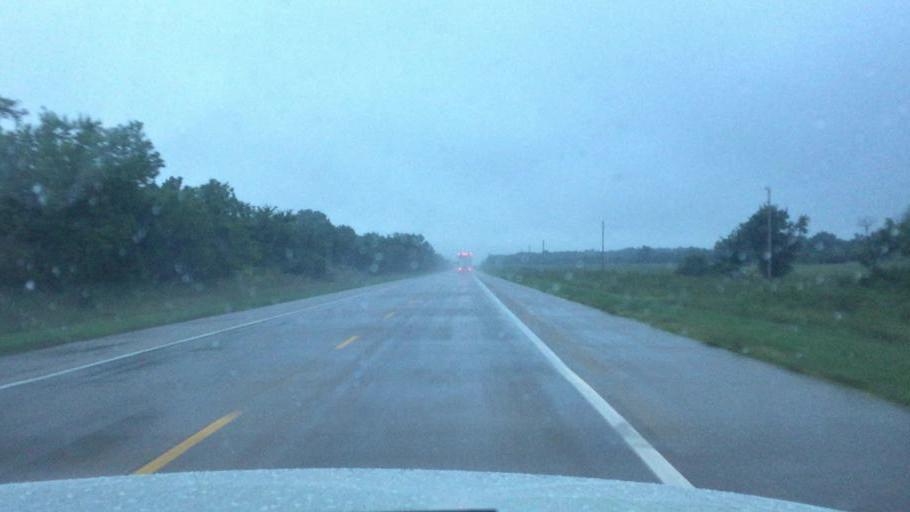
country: US
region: Kansas
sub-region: Neosho County
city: Chanute
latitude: 37.5563
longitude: -95.4709
